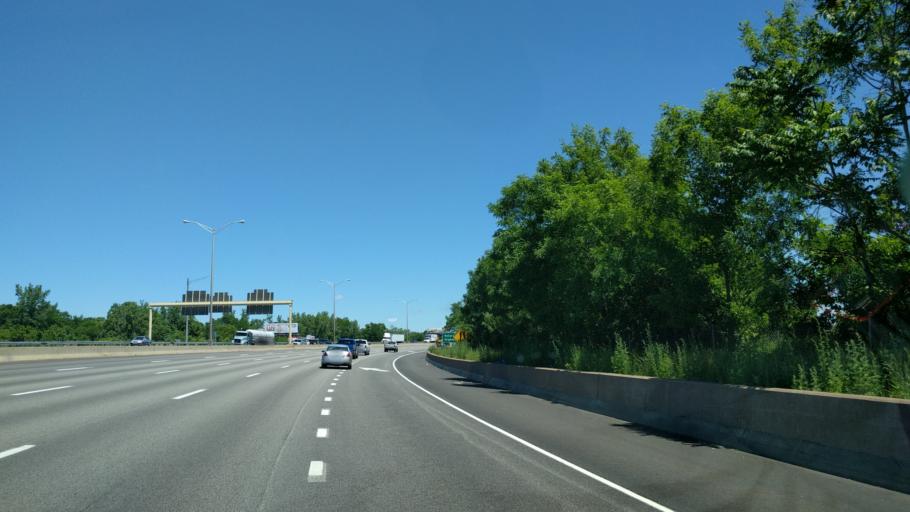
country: US
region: Connecticut
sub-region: Hartford County
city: Hartford
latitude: 41.7753
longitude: -72.6679
